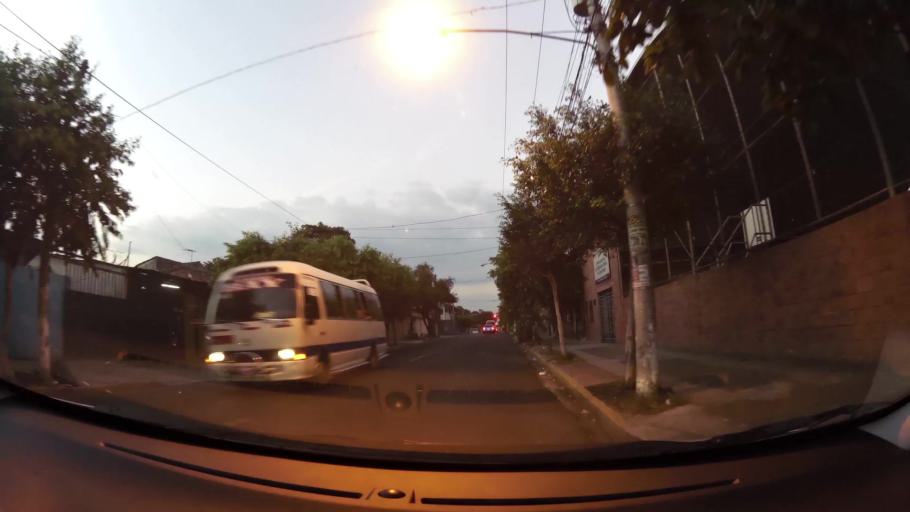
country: SV
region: San Salvador
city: San Salvador
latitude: 13.7083
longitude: -89.1860
